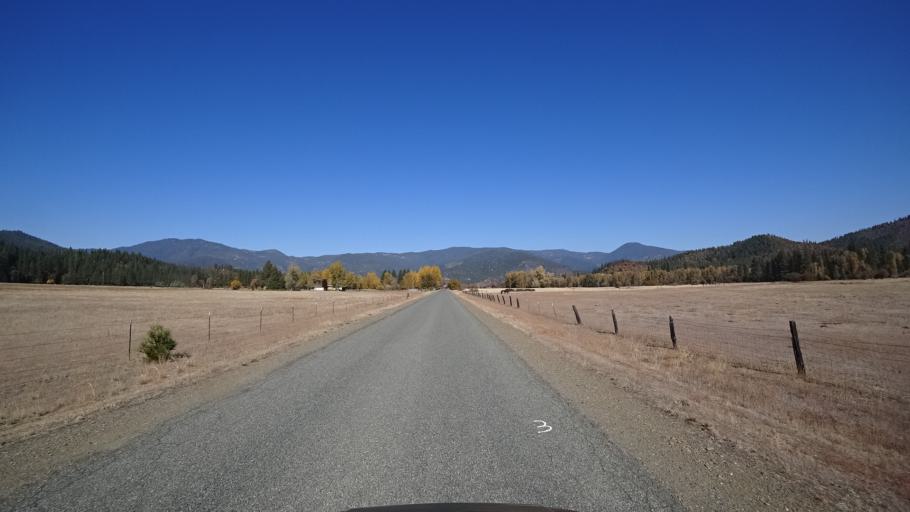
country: US
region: California
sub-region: Siskiyou County
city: Yreka
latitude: 41.6088
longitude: -122.9697
